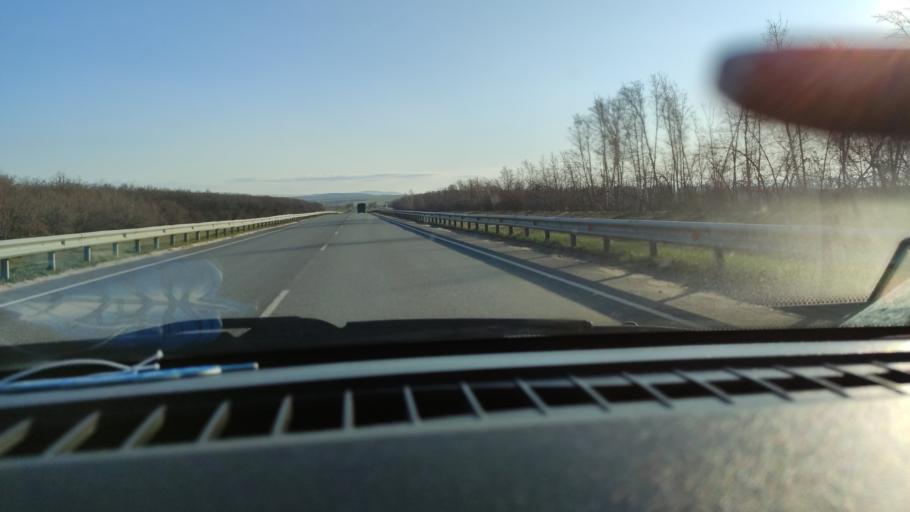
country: RU
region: Saratov
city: Balakovo
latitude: 52.1029
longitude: 47.7385
